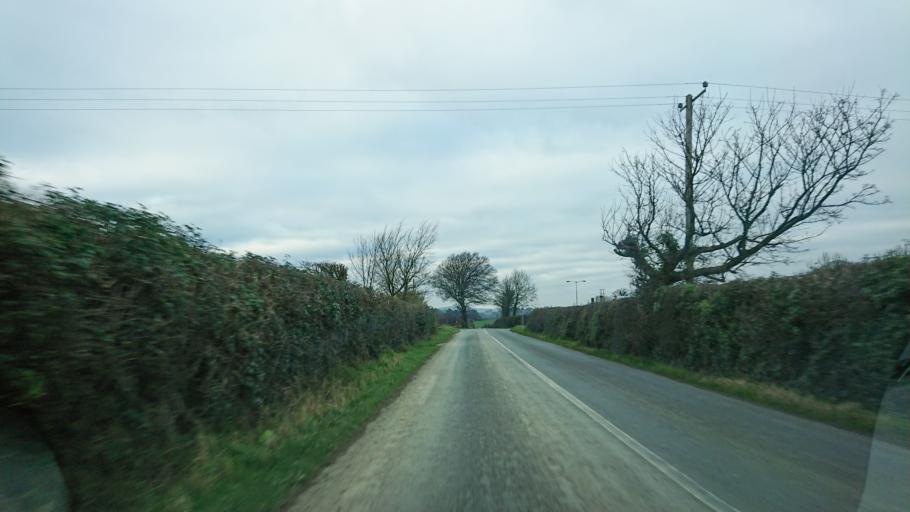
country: IE
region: Munster
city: Carrick-on-Suir
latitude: 52.2951
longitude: -7.4709
